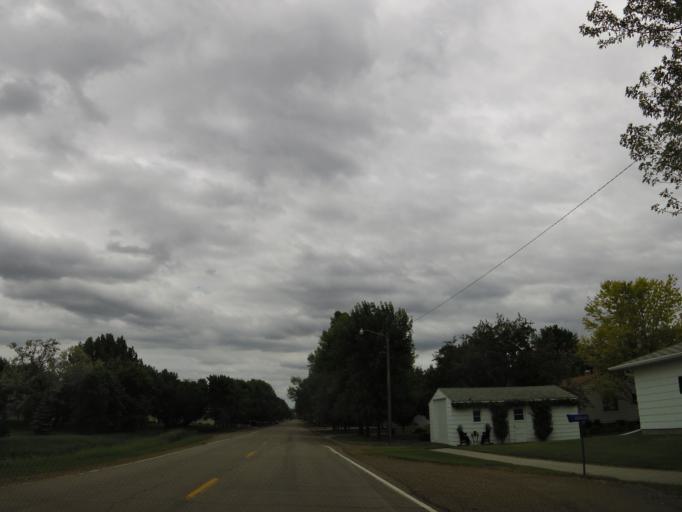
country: US
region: North Dakota
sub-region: Walsh County
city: Grafton
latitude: 48.6133
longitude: -97.4489
